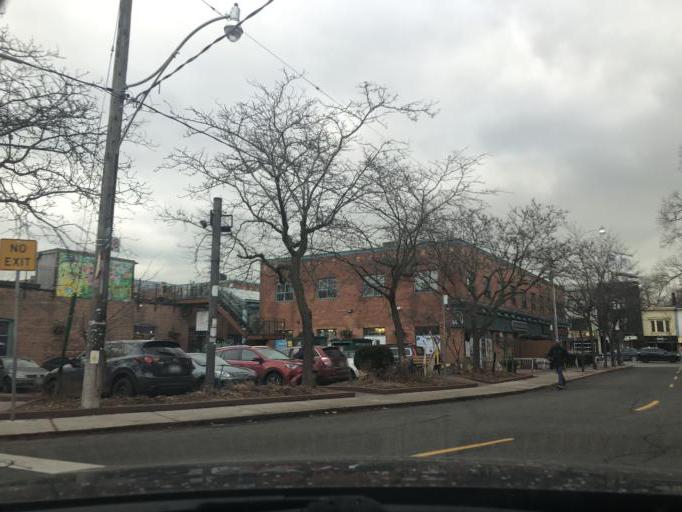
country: CA
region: Ontario
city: Toronto
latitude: 43.6780
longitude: -79.3536
